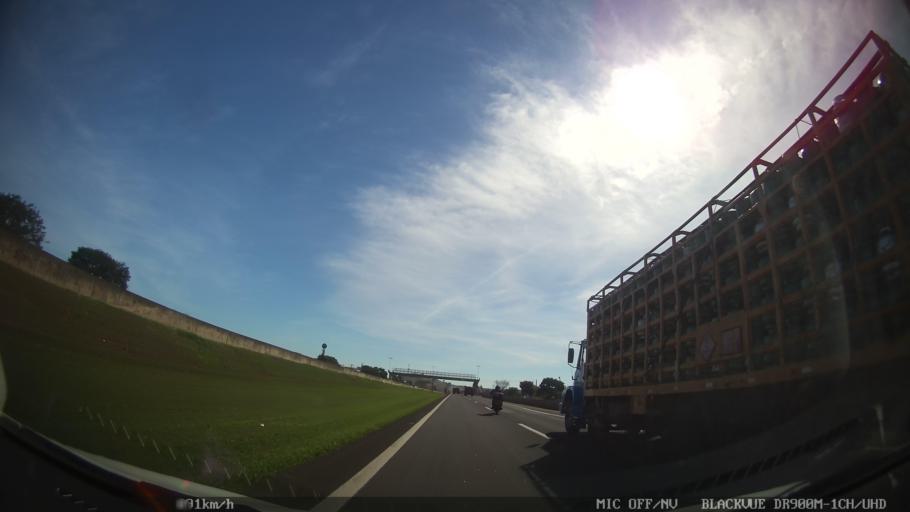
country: BR
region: Sao Paulo
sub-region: Leme
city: Leme
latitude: -22.1824
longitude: -47.3986
